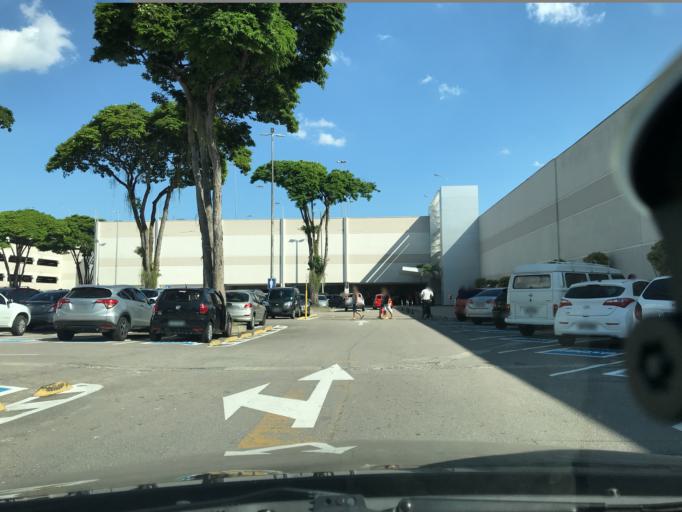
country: BR
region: Sao Paulo
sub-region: Sao Jose Dos Campos
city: Sao Jose dos Campos
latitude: -23.1989
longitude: -45.8824
